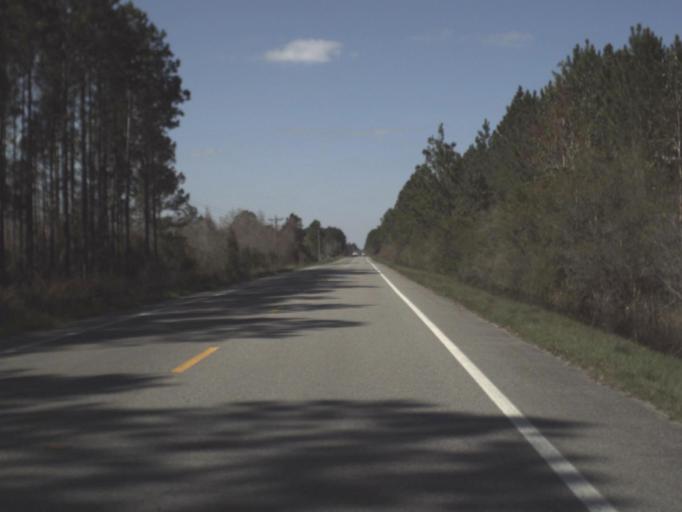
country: US
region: Florida
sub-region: Gulf County
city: Wewahitchka
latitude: 30.0193
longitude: -85.1781
